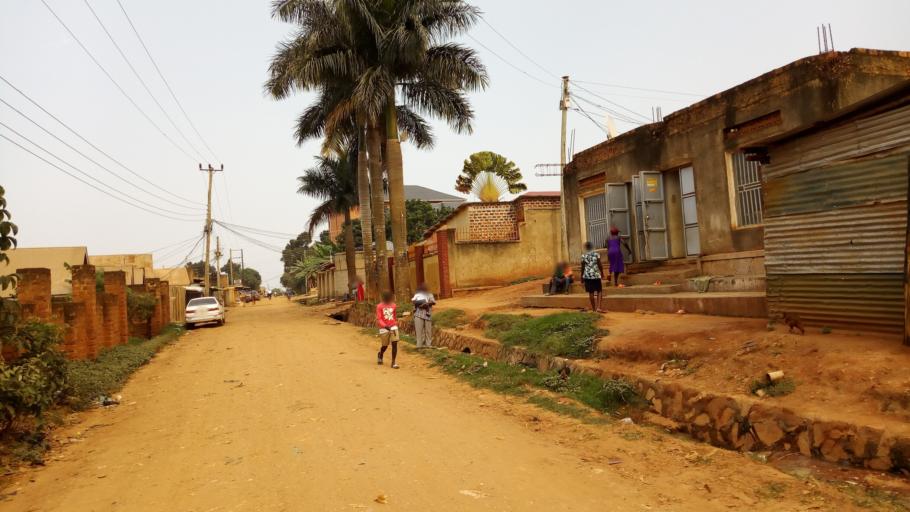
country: UG
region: Central Region
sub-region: Wakiso District
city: Kireka
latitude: 0.3186
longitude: 32.6468
